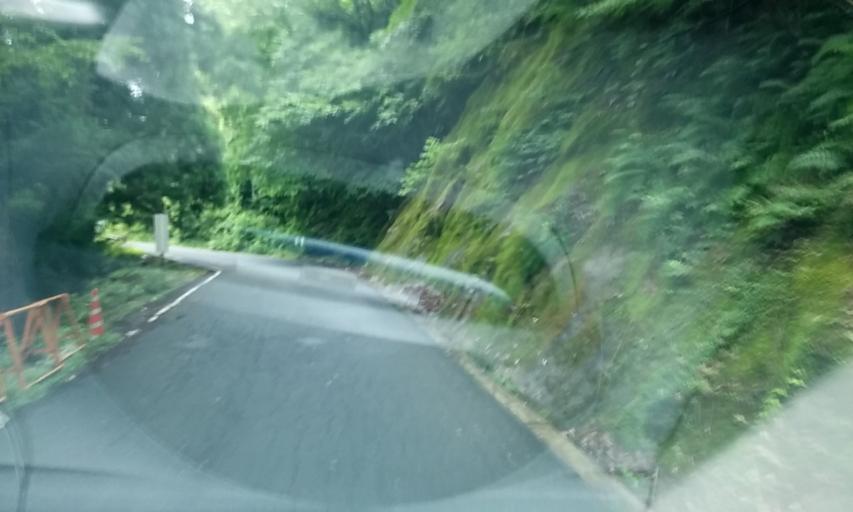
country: JP
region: Kyoto
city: Kameoka
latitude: 35.0543
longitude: 135.4263
